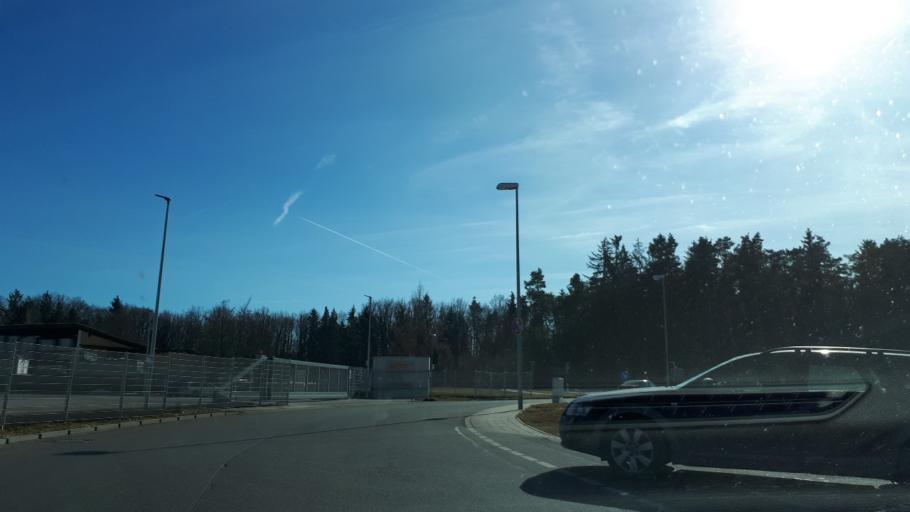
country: DE
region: Bavaria
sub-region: Upper Palatinate
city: Pentling
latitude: 48.9729
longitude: 12.0656
